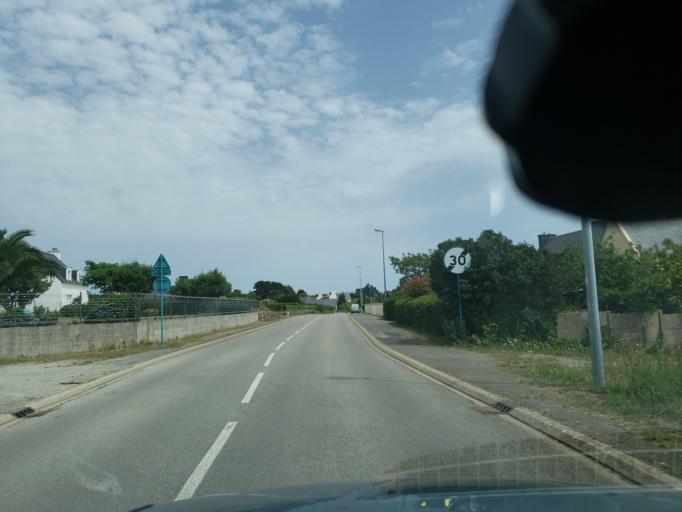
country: FR
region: Brittany
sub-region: Departement du Finistere
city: Treffiagat
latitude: 47.8003
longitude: -4.2570
